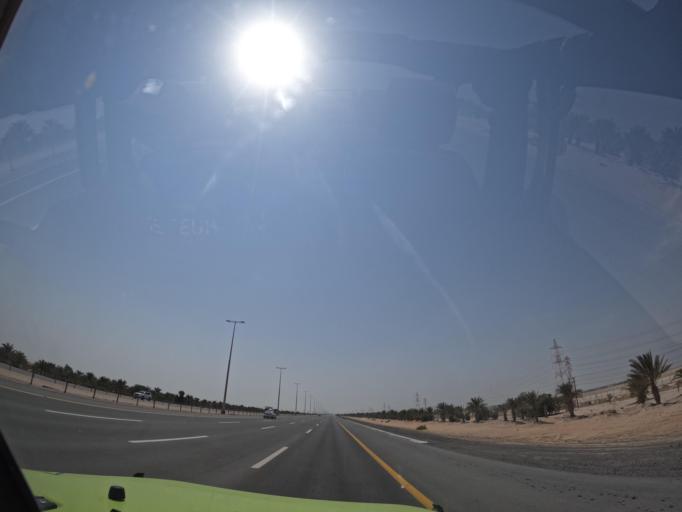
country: AE
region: Abu Dhabi
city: Abu Dhabi
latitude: 24.1929
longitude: 54.3883
